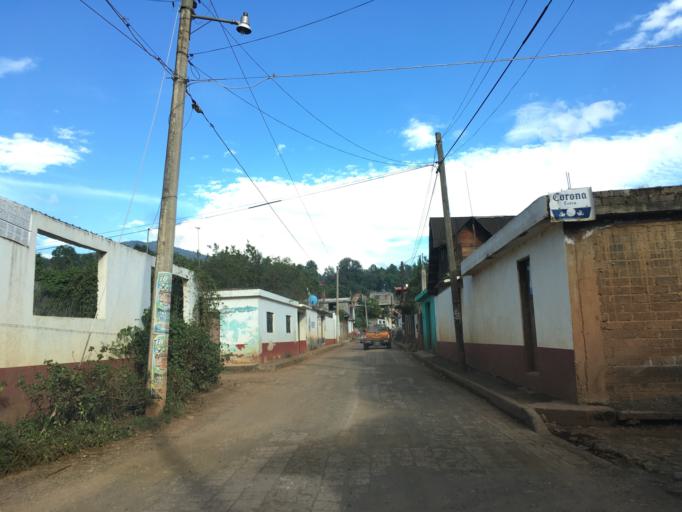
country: MX
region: Michoacan
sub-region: Patzcuaro
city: Santa Maria Huiramangaro (San Juan Tumbio)
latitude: 19.4529
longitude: -101.7300
